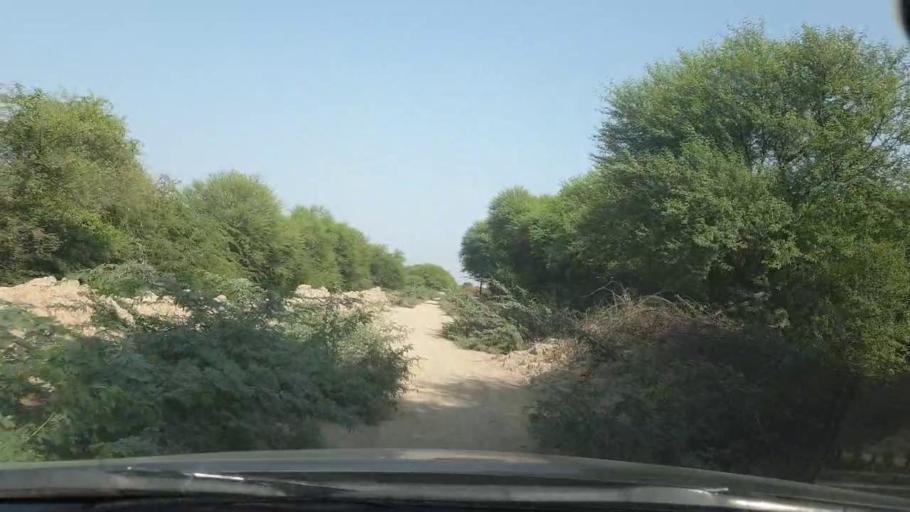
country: PK
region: Sindh
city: Naukot
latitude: 24.7987
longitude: 69.2581
